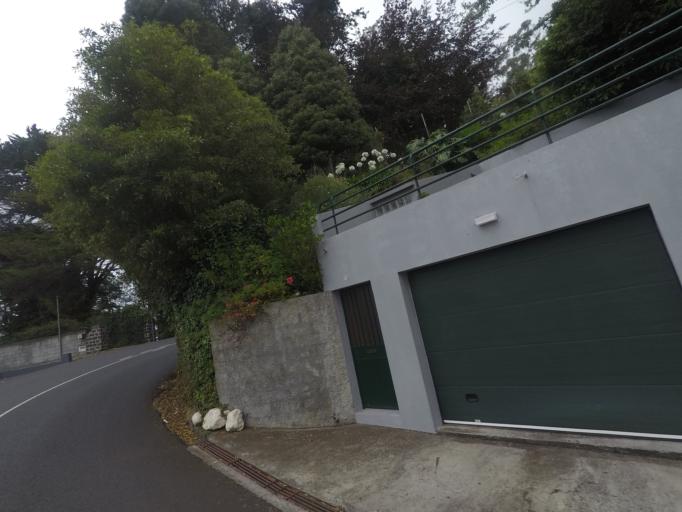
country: PT
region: Madeira
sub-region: Funchal
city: Nossa Senhora do Monte
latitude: 32.6651
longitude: -16.8737
